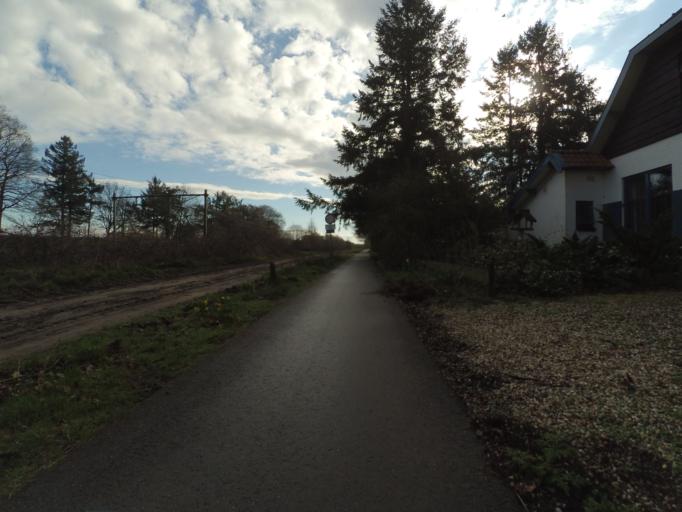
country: NL
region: Gelderland
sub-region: Gemeente Apeldoorn
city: Uddel
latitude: 52.2003
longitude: 5.8371
